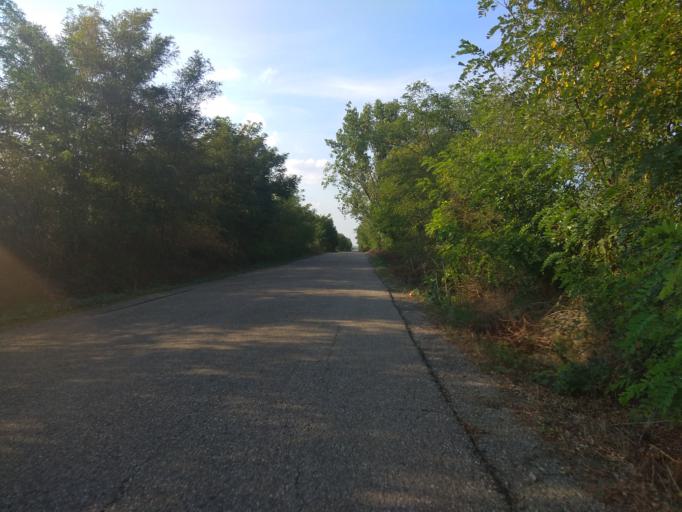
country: HU
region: Borsod-Abauj-Zemplen
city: Harsany
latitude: 47.9103
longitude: 20.7424
